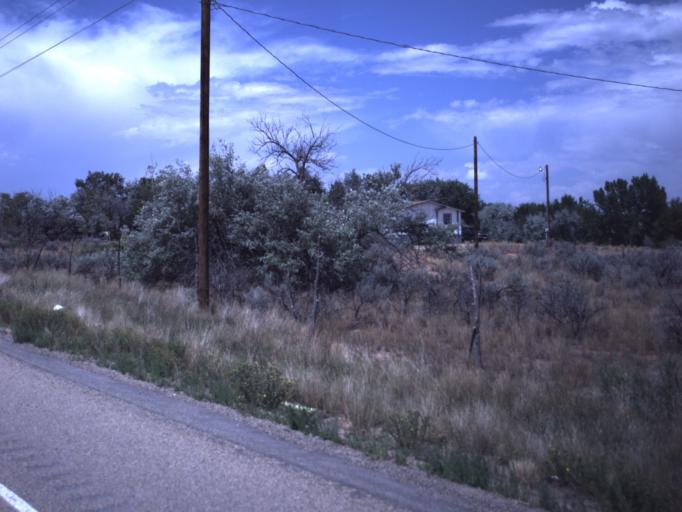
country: US
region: Utah
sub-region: Duchesne County
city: Roosevelt
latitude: 40.3020
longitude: -109.8693
